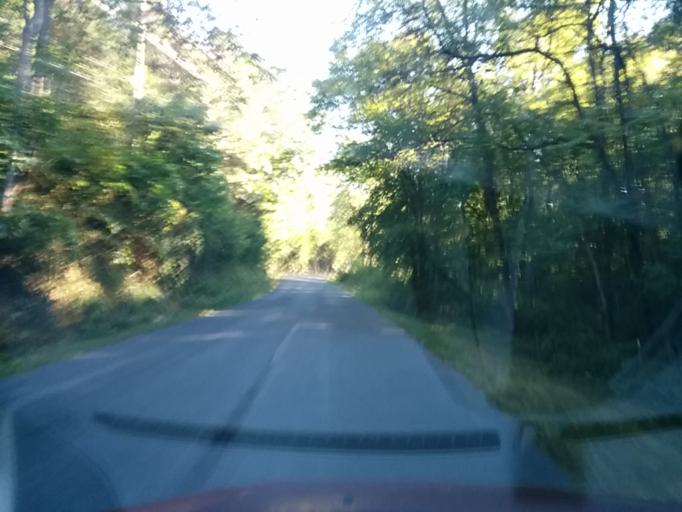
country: US
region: Virginia
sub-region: City of Lexington
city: Lexington
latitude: 37.7397
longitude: -79.5868
